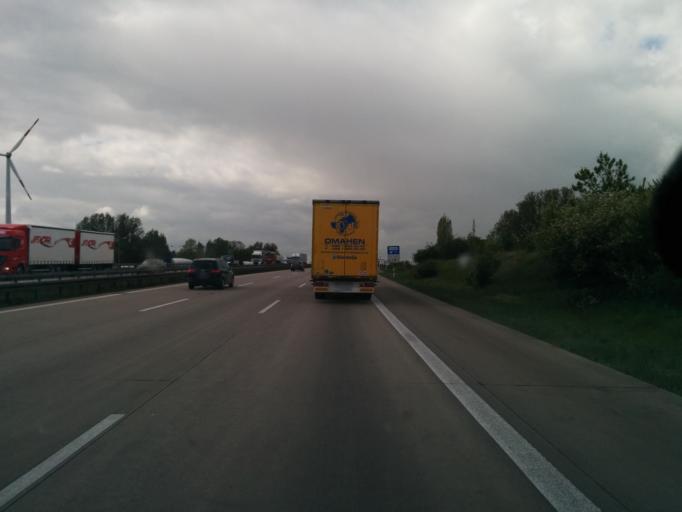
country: DE
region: Saxony-Anhalt
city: Hohenwarsleben
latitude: 52.1656
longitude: 11.5090
